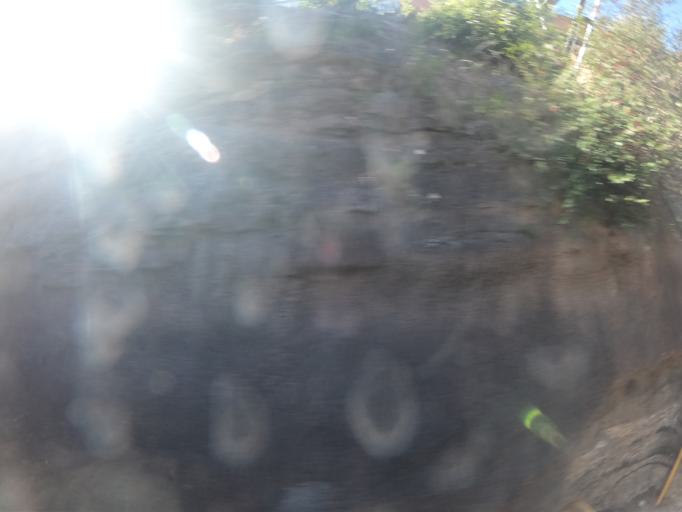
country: AU
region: New South Wales
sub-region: Hurstville
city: Oatley
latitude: -33.9763
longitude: 151.0785
